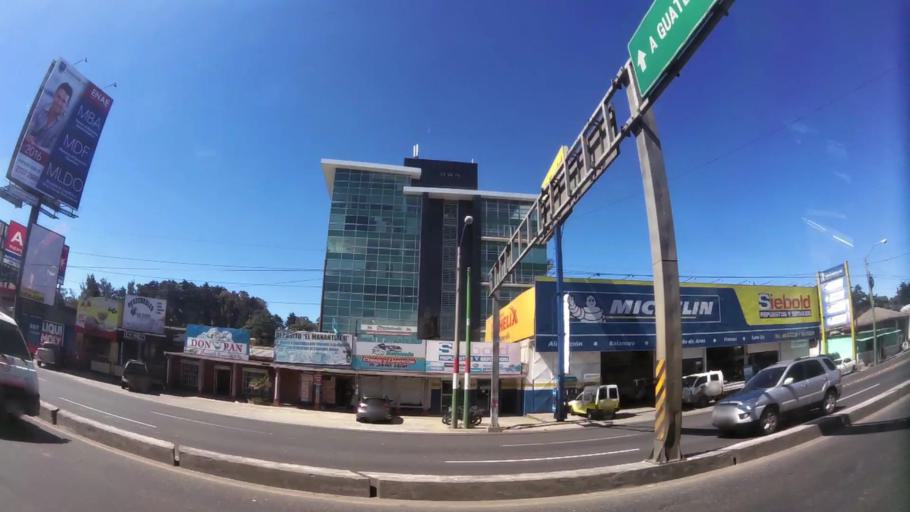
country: GT
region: Guatemala
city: San Jose Pinula
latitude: 14.5413
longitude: -90.4540
